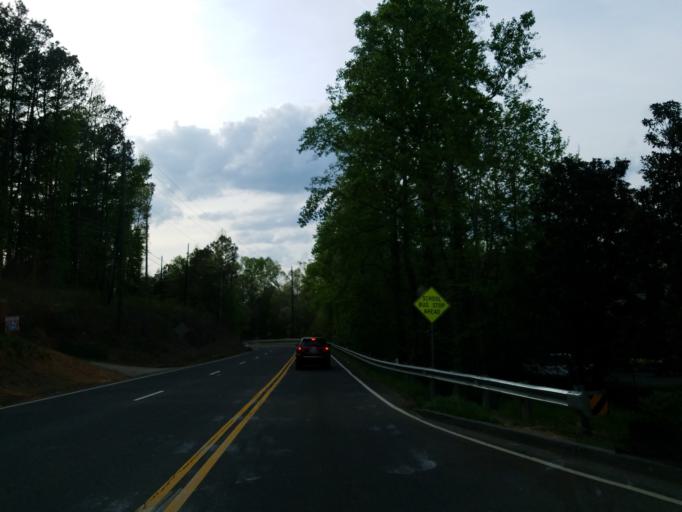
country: US
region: Georgia
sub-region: Cherokee County
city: Canton
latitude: 34.2240
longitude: -84.4755
